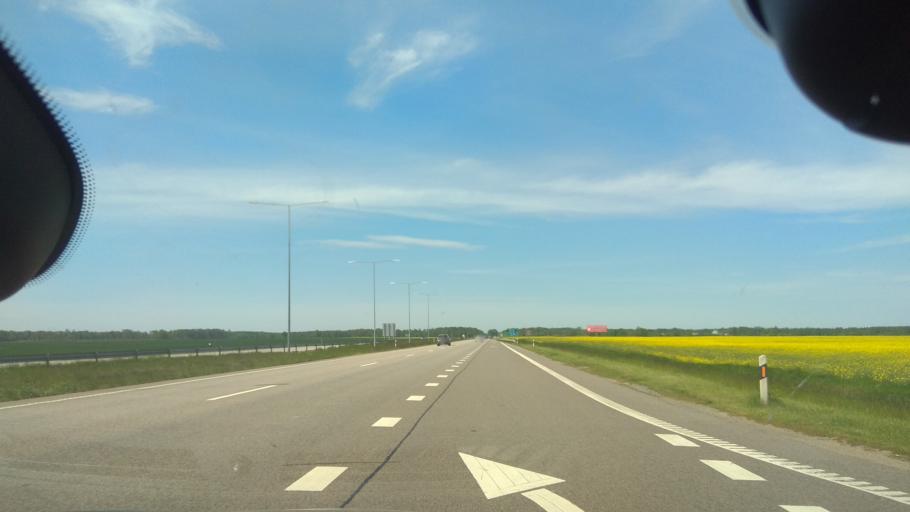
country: LT
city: Vilkija
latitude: 55.1419
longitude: 23.7193
